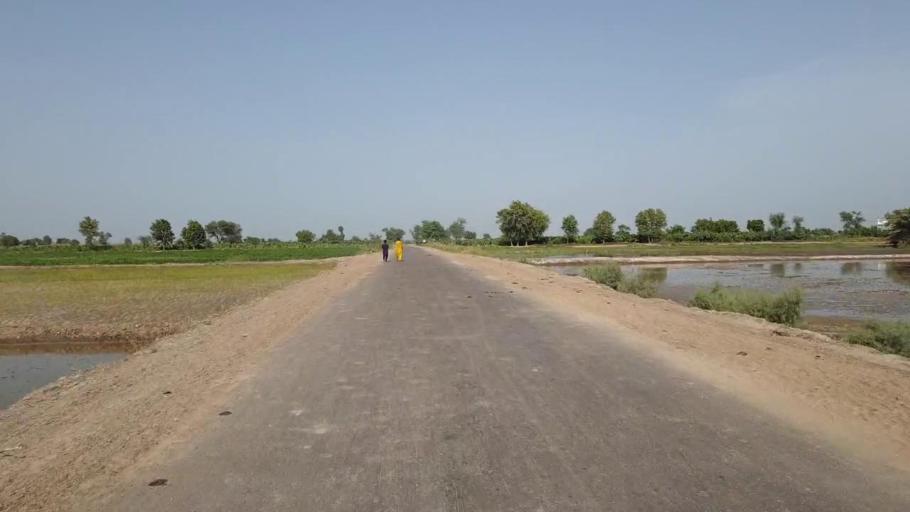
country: PK
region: Sindh
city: Sakrand
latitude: 26.2842
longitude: 68.2601
